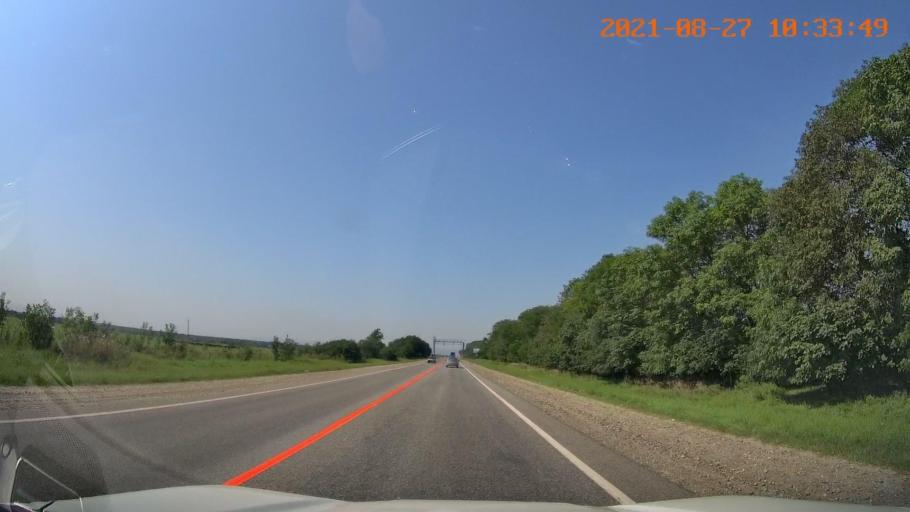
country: RU
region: Karachayevo-Cherkesiya
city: Cherkessk
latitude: 44.2579
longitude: 42.1159
